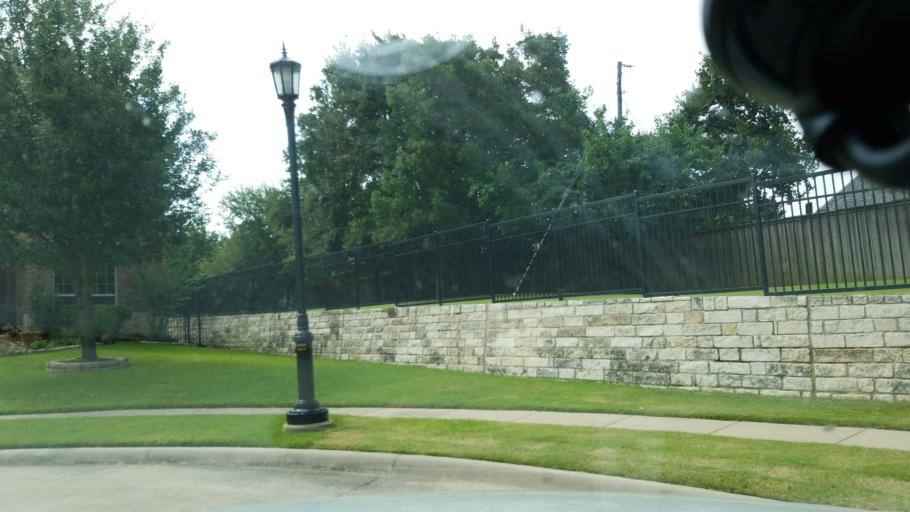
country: US
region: Texas
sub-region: Dallas County
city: Coppell
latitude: 32.9672
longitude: -96.9979
